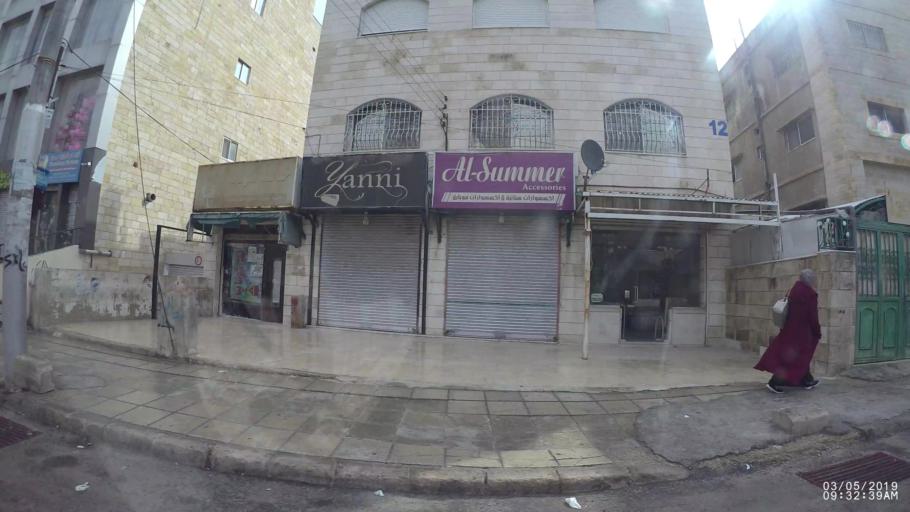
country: JO
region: Amman
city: Amman
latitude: 31.9801
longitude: 35.9245
